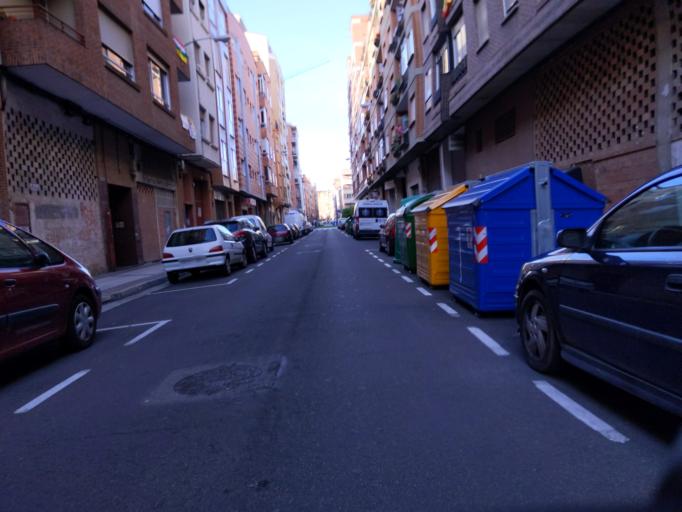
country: ES
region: La Rioja
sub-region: Provincia de La Rioja
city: Logrono
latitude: 42.4641
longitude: -2.4560
